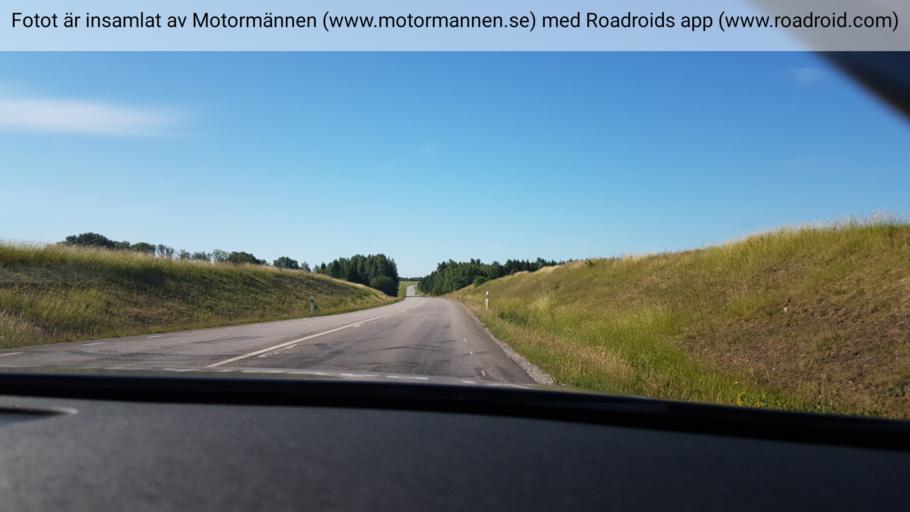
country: SE
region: Vaestra Goetaland
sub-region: Falkopings Kommun
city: Falkoeping
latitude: 58.1481
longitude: 13.5621
